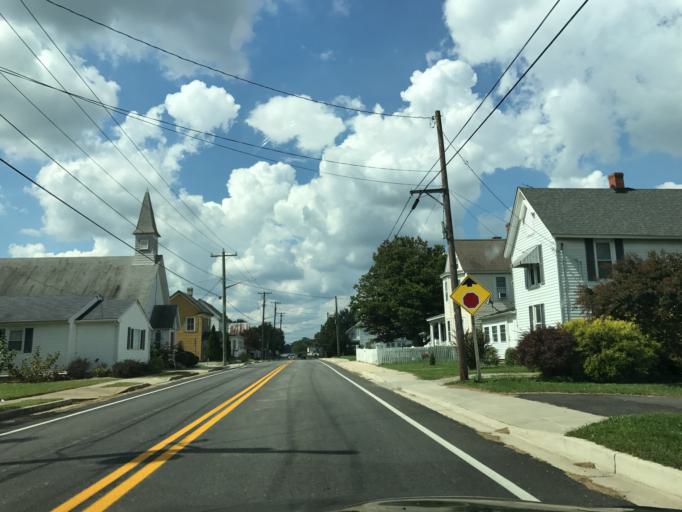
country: US
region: Maryland
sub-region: Caroline County
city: Greensboro
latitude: 39.1441
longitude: -75.8619
